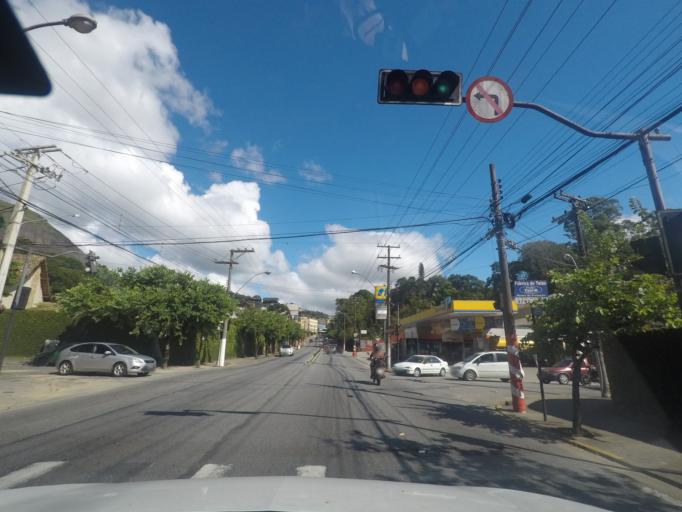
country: BR
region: Rio de Janeiro
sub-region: Teresopolis
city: Teresopolis
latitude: -22.4302
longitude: -42.9795
